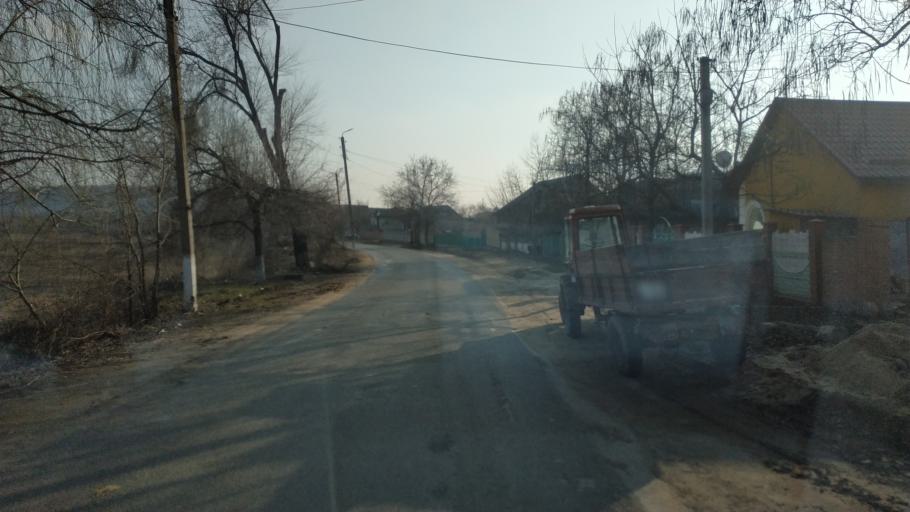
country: MD
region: Hincesti
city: Dancu
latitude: 46.7679
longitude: 28.3457
